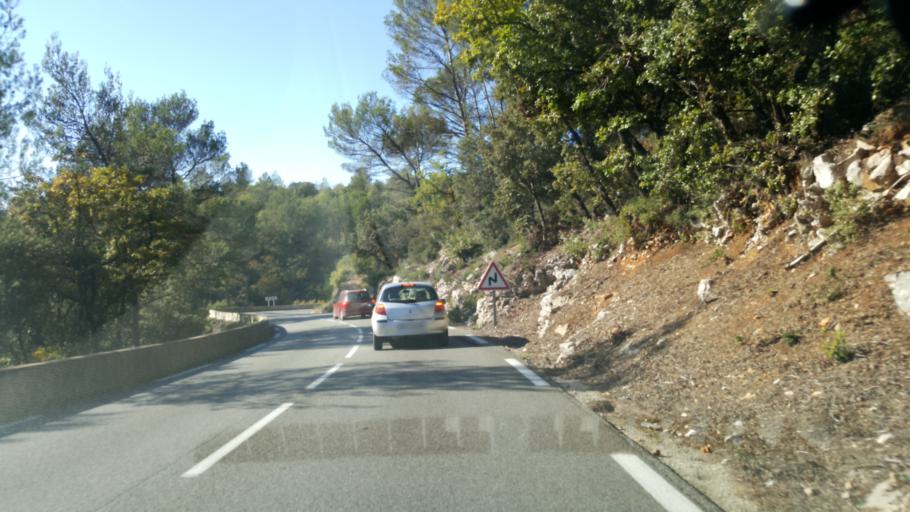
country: FR
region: Provence-Alpes-Cote d'Azur
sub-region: Departement du Var
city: Saint-Zacharie
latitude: 43.3857
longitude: 5.7458
